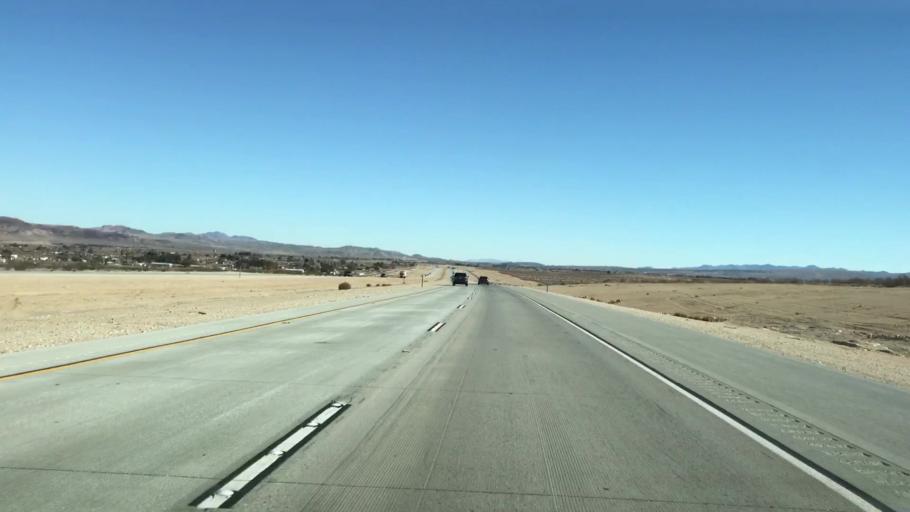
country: US
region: California
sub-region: San Bernardino County
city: Lenwood
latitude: 34.9137
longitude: -117.2284
